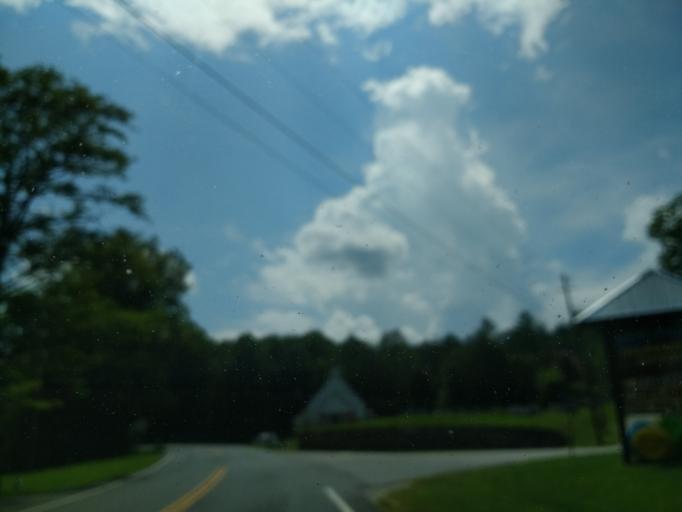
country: US
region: Georgia
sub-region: White County
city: Cleveland
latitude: 34.7127
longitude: -83.7469
